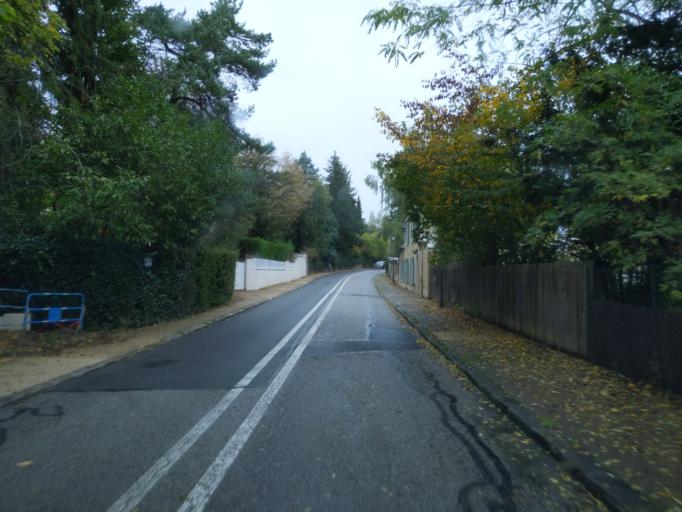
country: FR
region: Ile-de-France
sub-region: Departement des Yvelines
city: Dampierre-en-Yvelines
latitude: 48.7011
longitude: 1.9810
